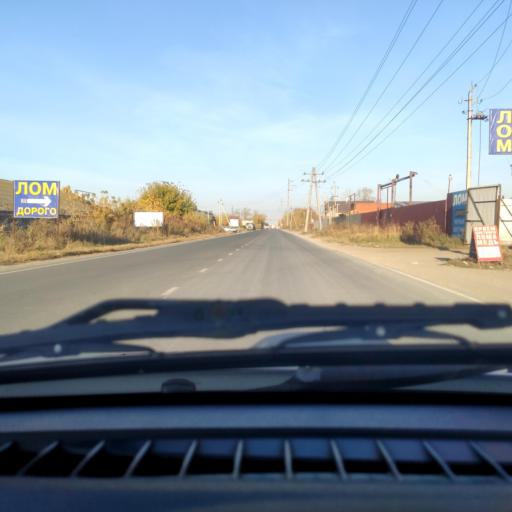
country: RU
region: Samara
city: Zhigulevsk
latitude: 53.5254
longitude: 49.4841
